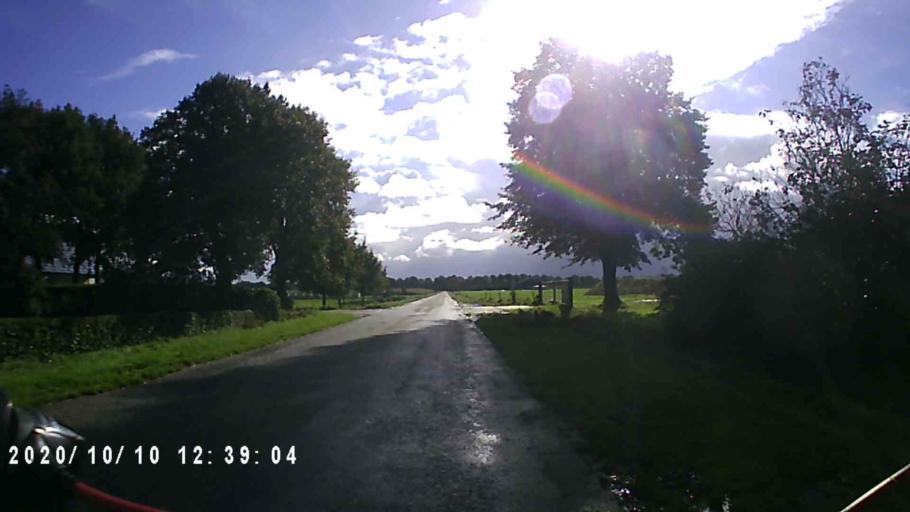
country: NL
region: Friesland
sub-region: Gemeente Weststellingwerf
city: Noordwolde
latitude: 52.9461
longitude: 6.2078
